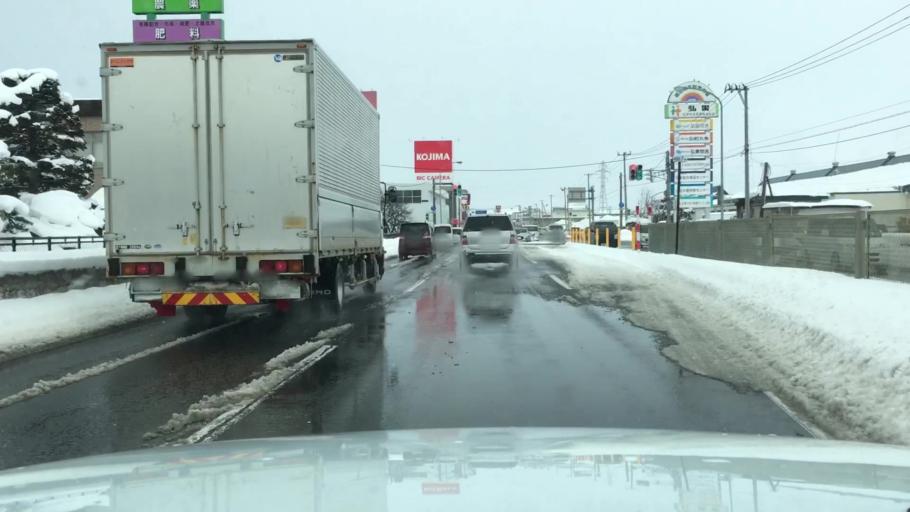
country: JP
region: Aomori
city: Hirosaki
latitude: 40.6056
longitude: 140.4990
